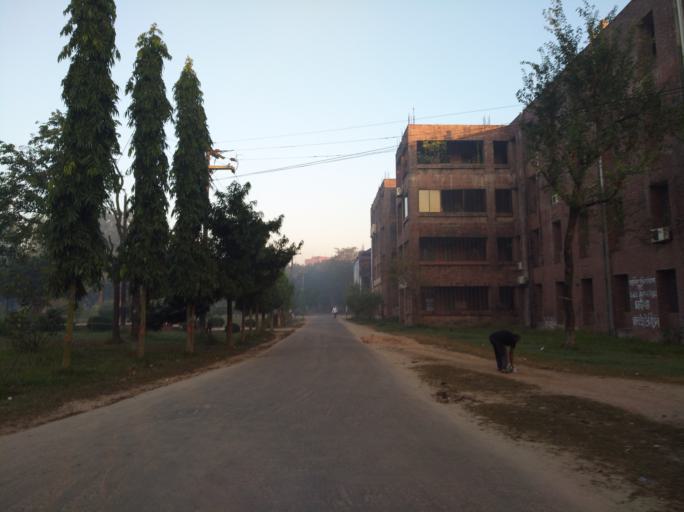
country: BD
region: Dhaka
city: Tungi
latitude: 23.8799
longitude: 90.2687
